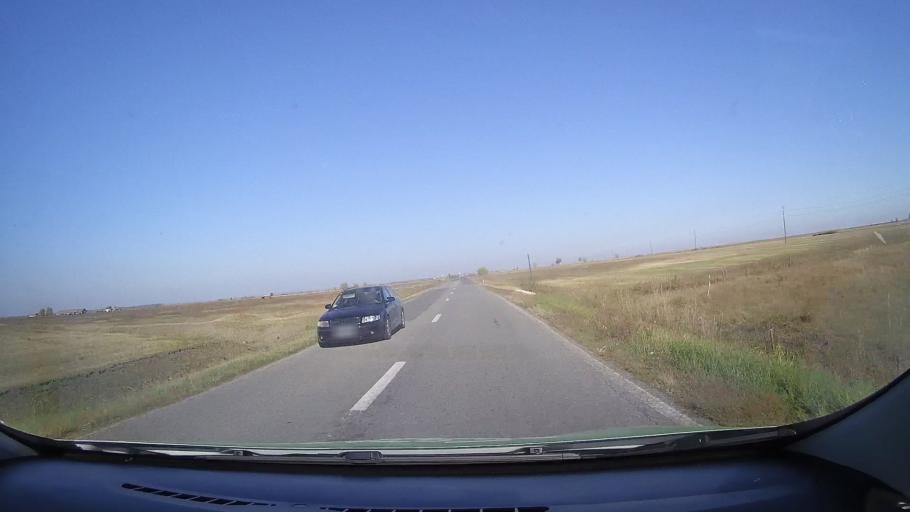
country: RO
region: Satu Mare
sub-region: Comuna Cauas
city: Cauas
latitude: 47.5459
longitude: 22.5624
